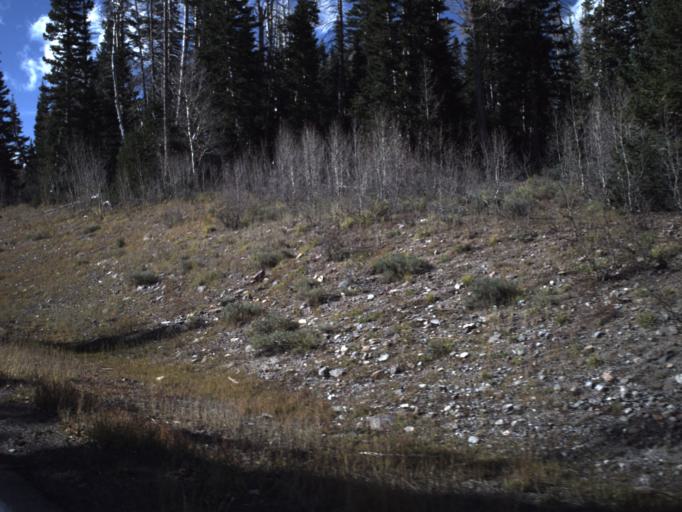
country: US
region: Utah
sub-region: Iron County
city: Parowan
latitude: 37.6504
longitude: -112.7900
